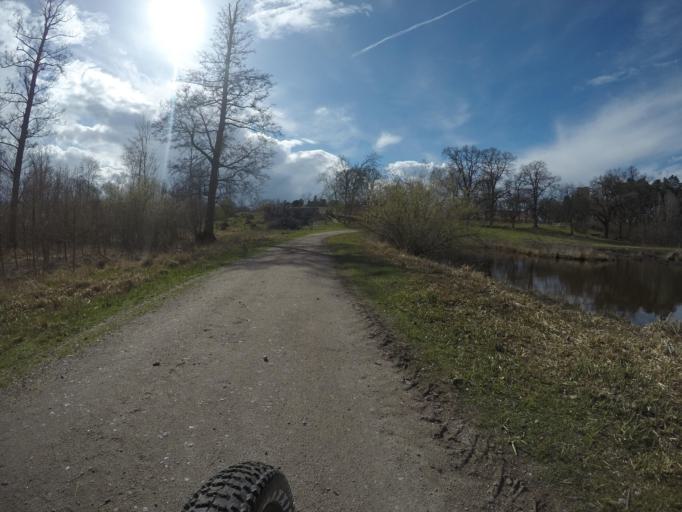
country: SE
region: Vaestmanland
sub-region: Kungsors Kommun
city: Kungsoer
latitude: 59.2722
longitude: 16.1256
